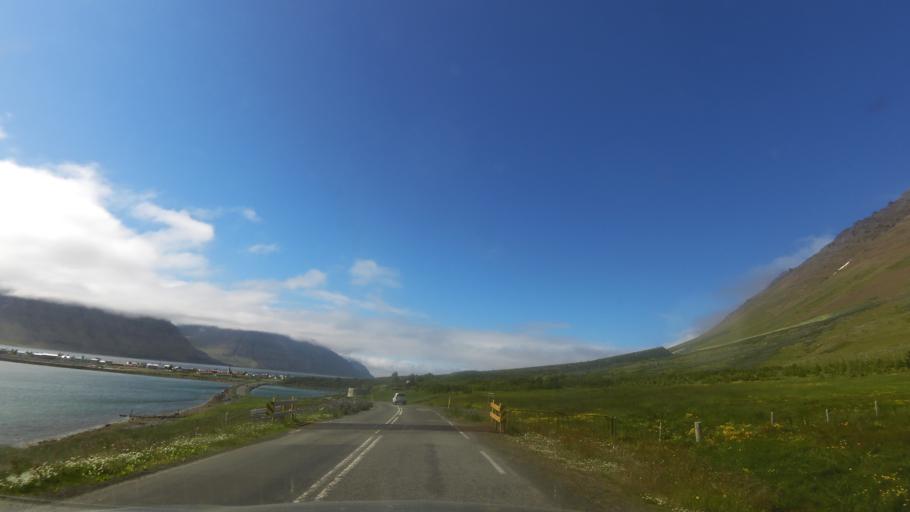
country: IS
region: Westfjords
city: Isafjoerdur
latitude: 66.0516
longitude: -23.4927
